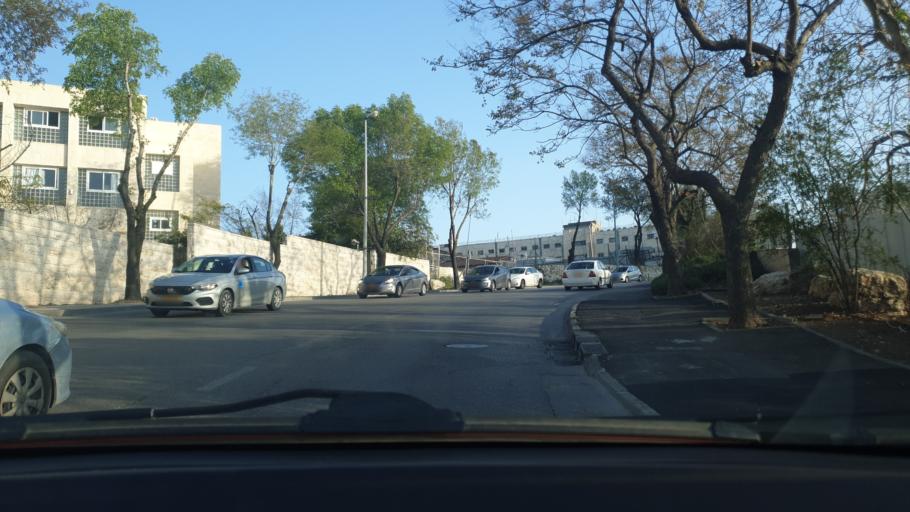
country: PS
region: West Bank
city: Bayt Iksa
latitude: 31.7887
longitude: 35.1896
